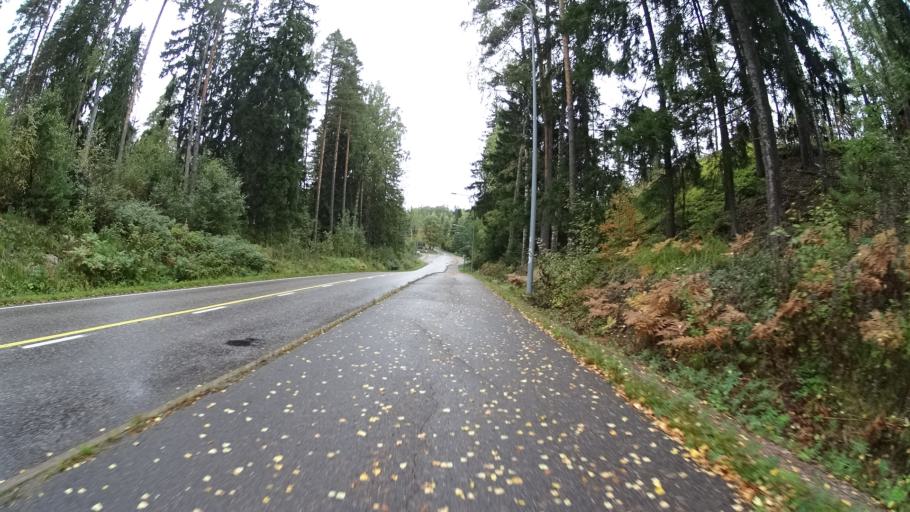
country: FI
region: Uusimaa
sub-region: Helsinki
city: Espoo
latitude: 60.2487
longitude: 24.6556
